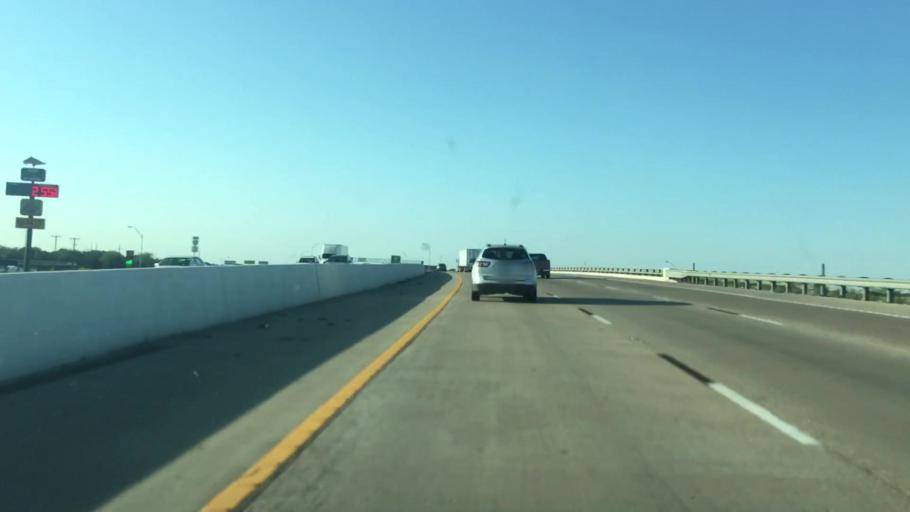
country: US
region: Texas
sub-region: McLennan County
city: Northcrest
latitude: 31.6530
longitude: -97.1009
